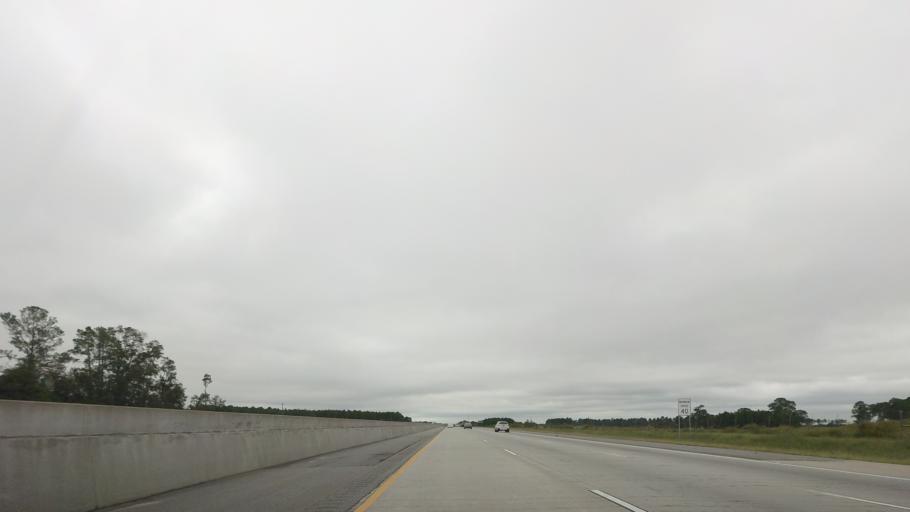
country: US
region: Georgia
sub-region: Tift County
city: Unionville
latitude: 31.3459
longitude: -83.4869
